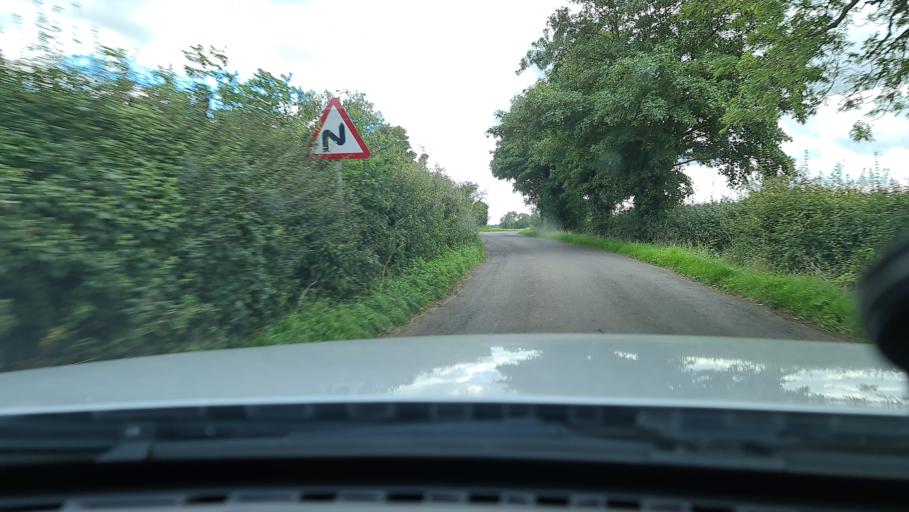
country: GB
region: England
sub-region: Oxfordshire
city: Somerton
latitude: 51.9612
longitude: -1.2635
